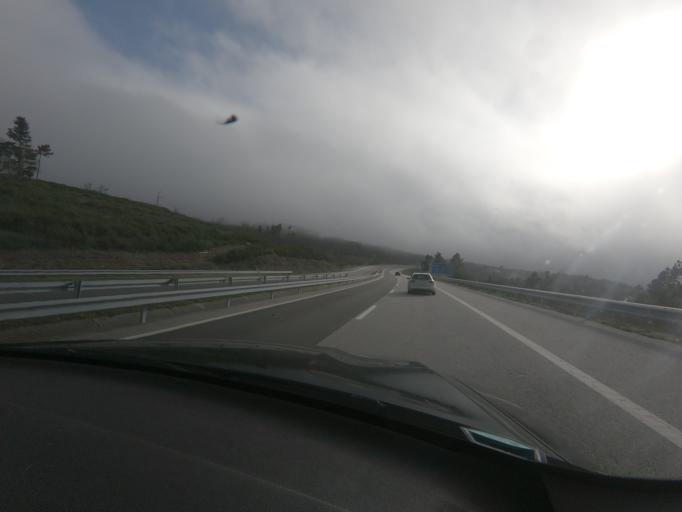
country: PT
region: Viseu
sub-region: Castro Daire
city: Castro Daire
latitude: 40.9871
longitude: -7.8835
